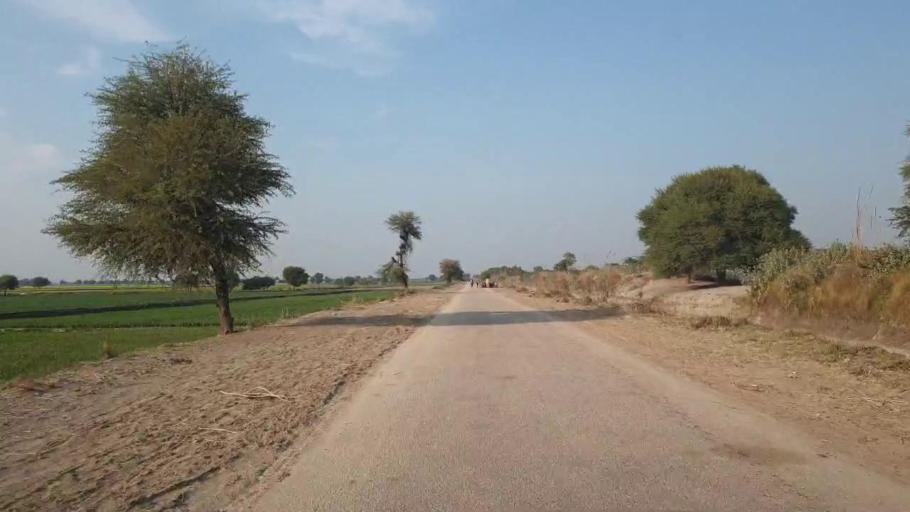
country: PK
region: Sindh
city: Shahpur Chakar
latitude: 26.1635
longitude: 68.6406
